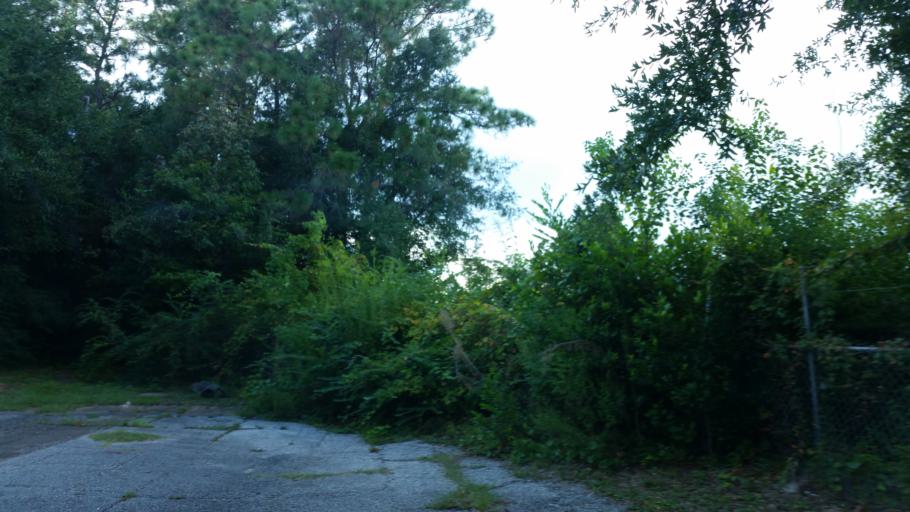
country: US
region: Florida
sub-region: Escambia County
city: Ferry Pass
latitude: 30.5018
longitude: -87.1773
